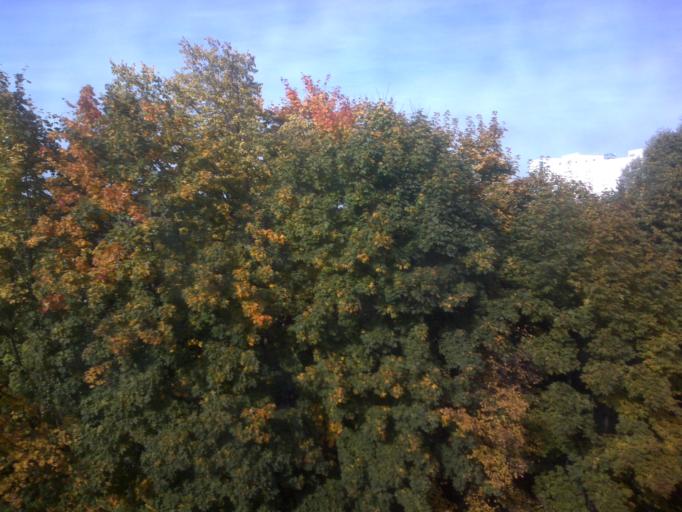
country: RU
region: Moscow
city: Annino
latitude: 55.5694
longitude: 37.6096
